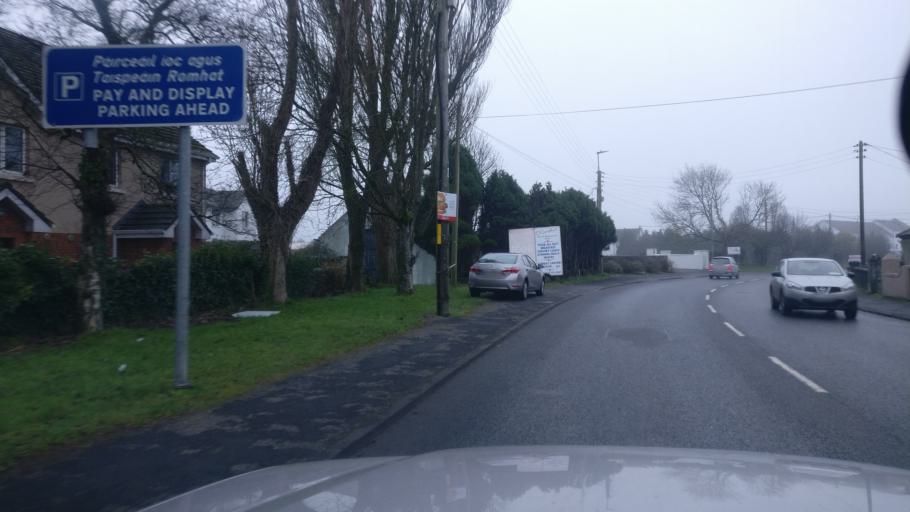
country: IE
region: Connaught
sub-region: County Galway
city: Gort
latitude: 53.0714
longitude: -8.8229
